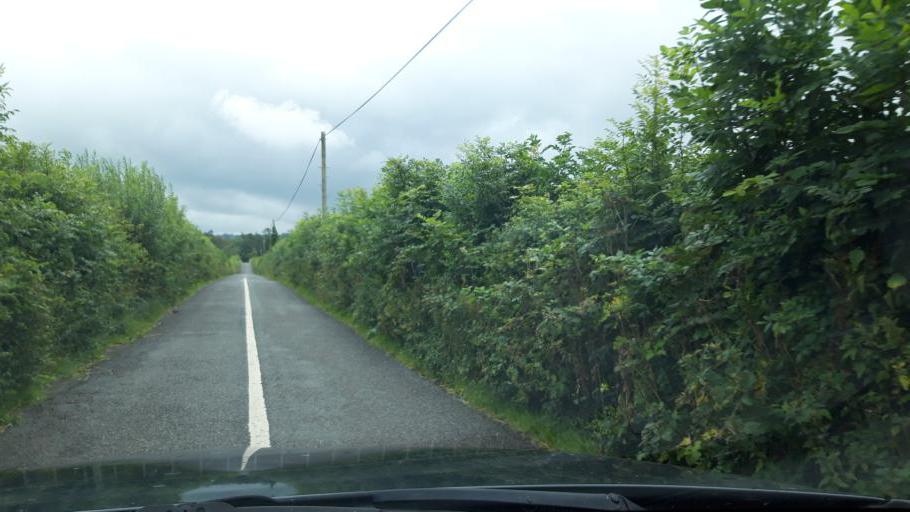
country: IE
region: Munster
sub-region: County Cork
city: Castlemartyr
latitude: 52.1346
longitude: -8.0113
